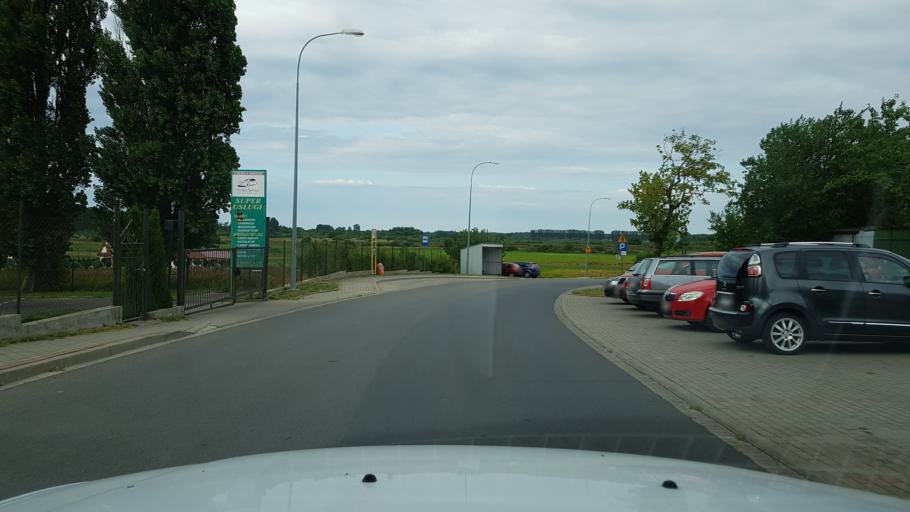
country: PL
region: West Pomeranian Voivodeship
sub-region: Powiat kolobrzeski
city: Kolobrzeg
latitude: 54.1672
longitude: 15.6030
